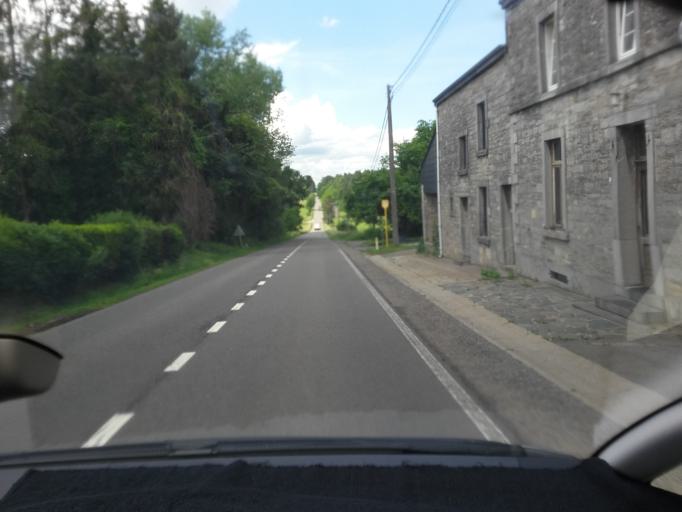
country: BE
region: Wallonia
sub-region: Province de Namur
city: Rochefort
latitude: 50.1278
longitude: 5.2400
